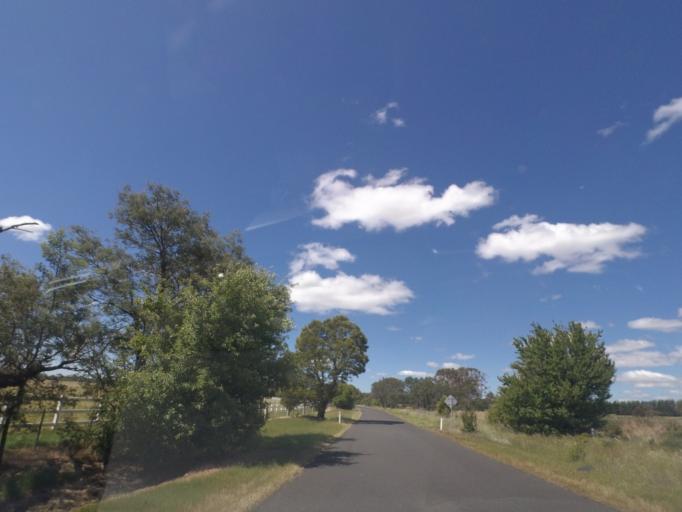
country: AU
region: Victoria
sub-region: Moorabool
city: Bacchus Marsh
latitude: -37.3357
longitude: 144.4407
